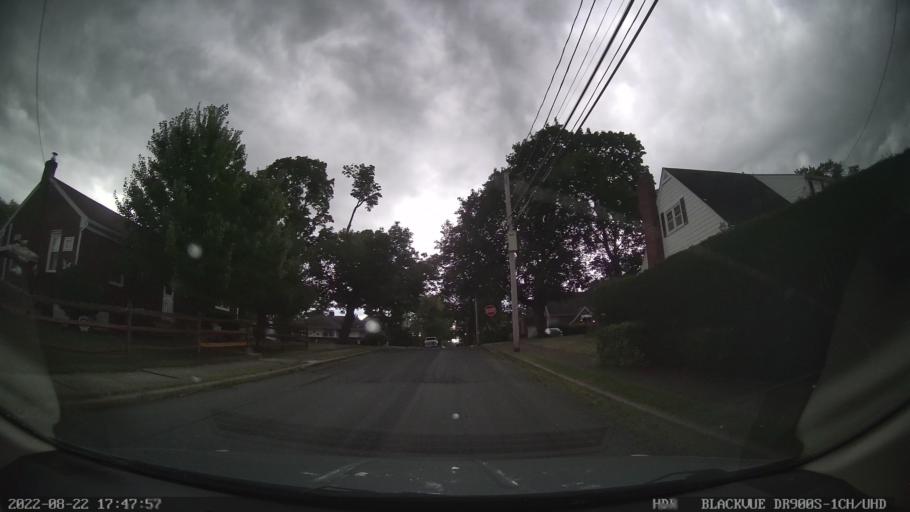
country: US
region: Pennsylvania
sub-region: Lehigh County
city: Allentown
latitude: 40.5913
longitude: -75.5028
